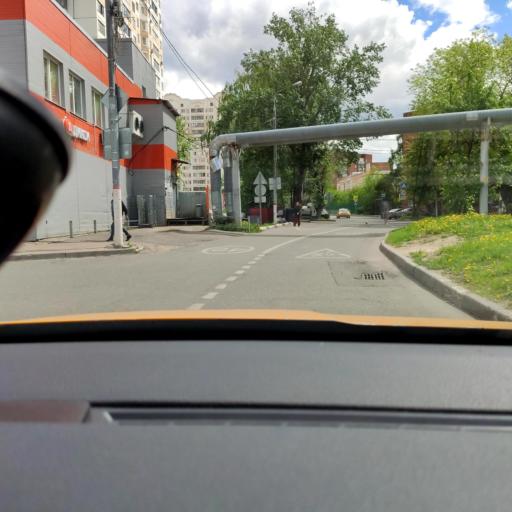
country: RU
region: Moskovskaya
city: Novopodrezkovo
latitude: 55.9417
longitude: 37.3459
